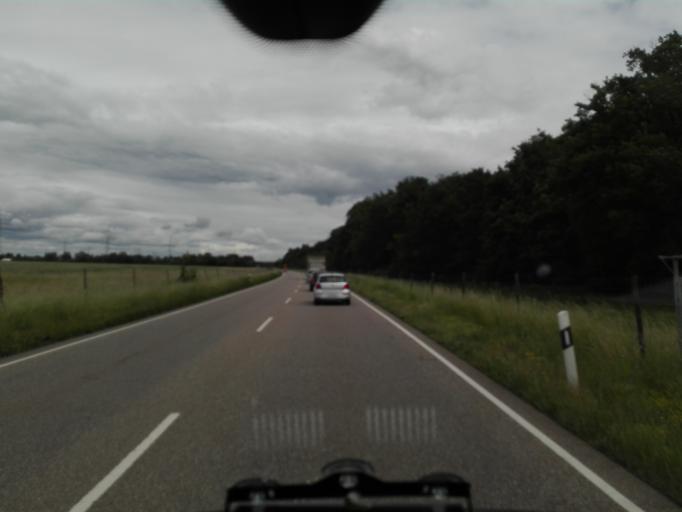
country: DE
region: Baden-Wuerttemberg
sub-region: Karlsruhe Region
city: Linkenheim-Hochstetten
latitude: 49.1128
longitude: 8.4279
